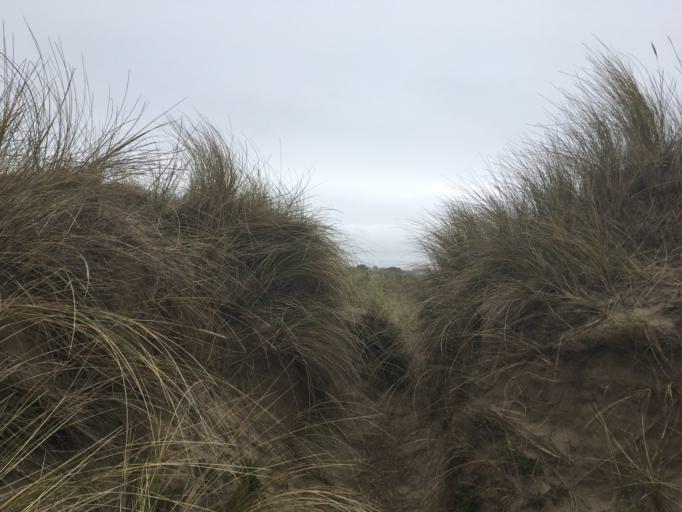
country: IE
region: Leinster
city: Portmarnock
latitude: 53.4207
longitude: -6.1221
